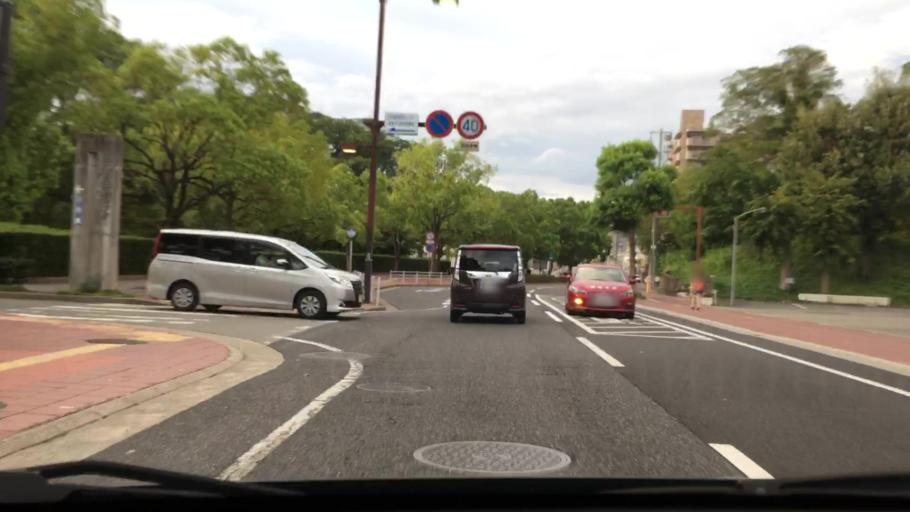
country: JP
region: Hyogo
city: Himeji
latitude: 34.8413
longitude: 134.6982
